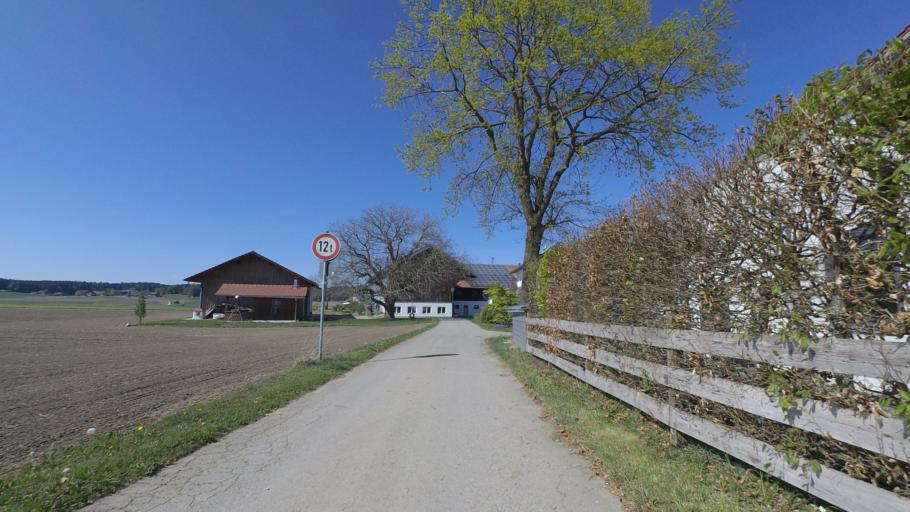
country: DE
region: Bavaria
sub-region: Upper Bavaria
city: Traunreut
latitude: 47.9581
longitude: 12.5321
